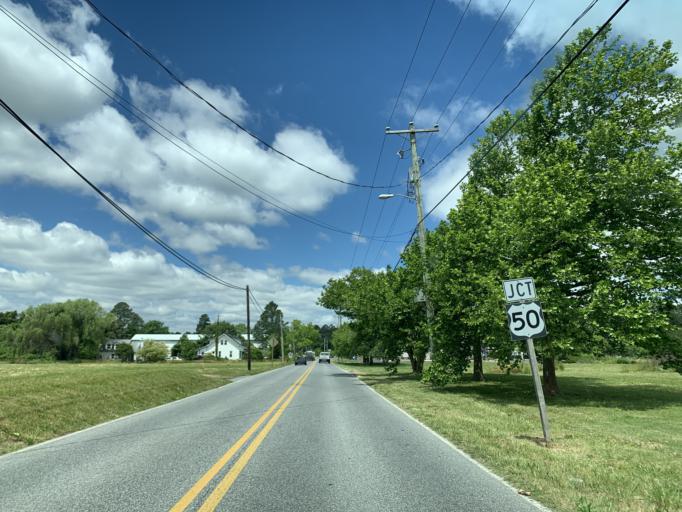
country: US
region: Maryland
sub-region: Worcester County
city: West Ocean City
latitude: 38.3379
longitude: -75.1240
